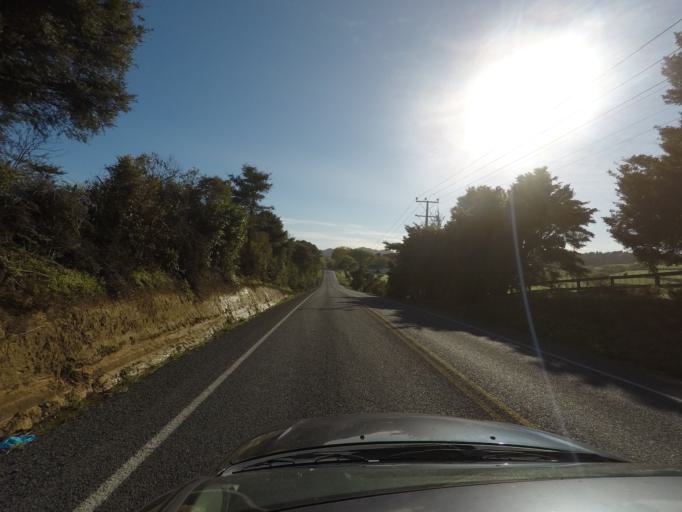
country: NZ
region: Auckland
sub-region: Auckland
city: Red Hill
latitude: -36.9912
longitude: 174.9873
